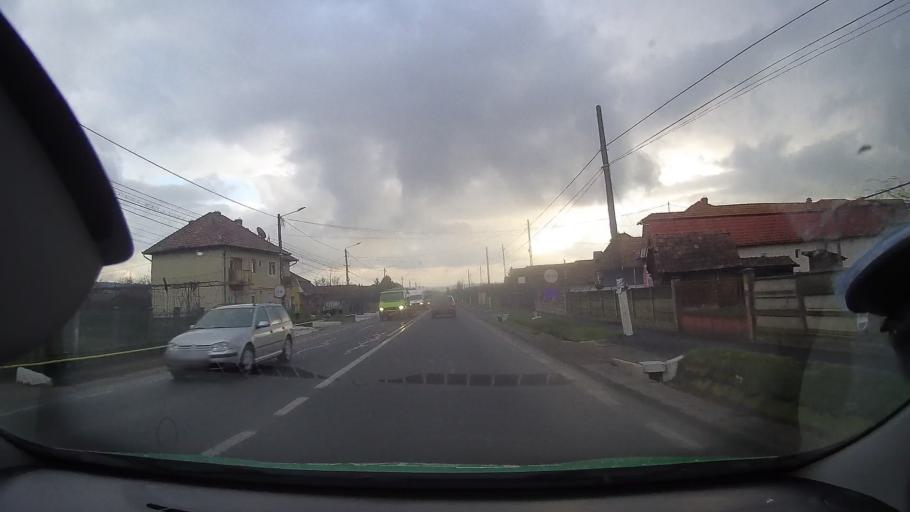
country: RO
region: Cluj
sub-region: Comuna Luna
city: Luncani
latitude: 46.4977
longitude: 23.9249
